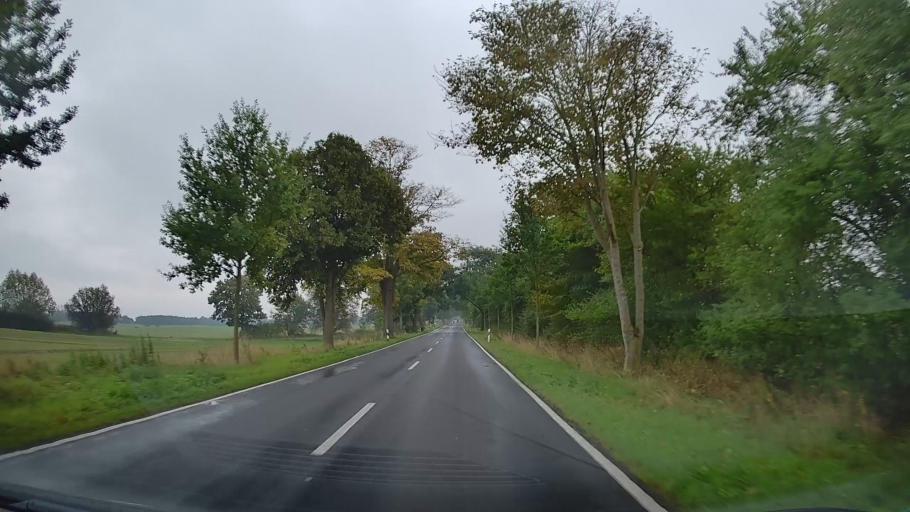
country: DE
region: Mecklenburg-Vorpommern
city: Ostseebad Boltenhagen
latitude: 53.9479
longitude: 11.2336
